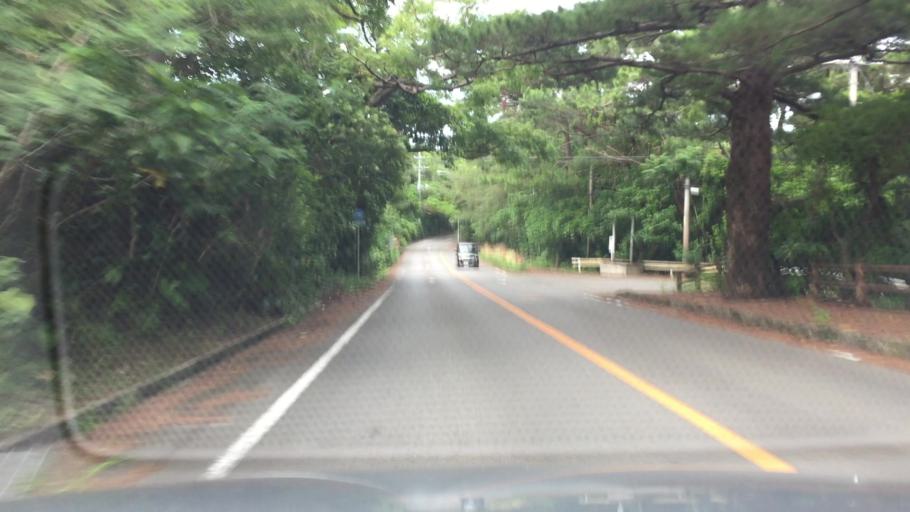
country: JP
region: Okinawa
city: Ishigaki
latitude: 24.4494
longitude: 124.1337
